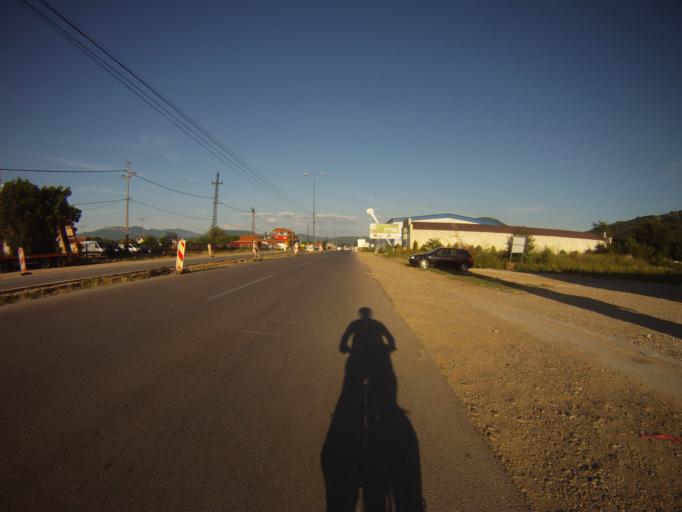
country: RS
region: Central Serbia
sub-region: Nisavski Okrug
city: Niska Banja
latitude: 43.3058
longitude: 21.9630
